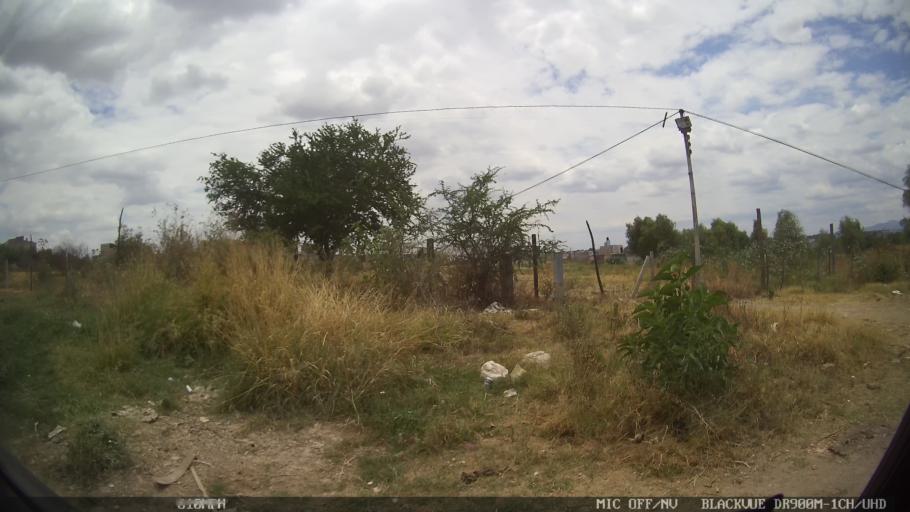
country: MX
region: Jalisco
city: Tlaquepaque
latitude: 20.6398
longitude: -103.2706
